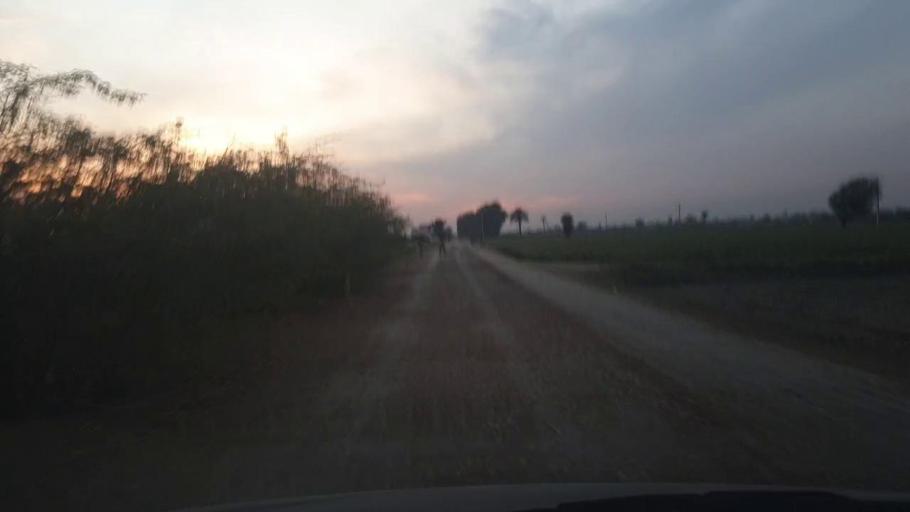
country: PK
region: Sindh
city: Kunri
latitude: 25.2240
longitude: 69.5305
